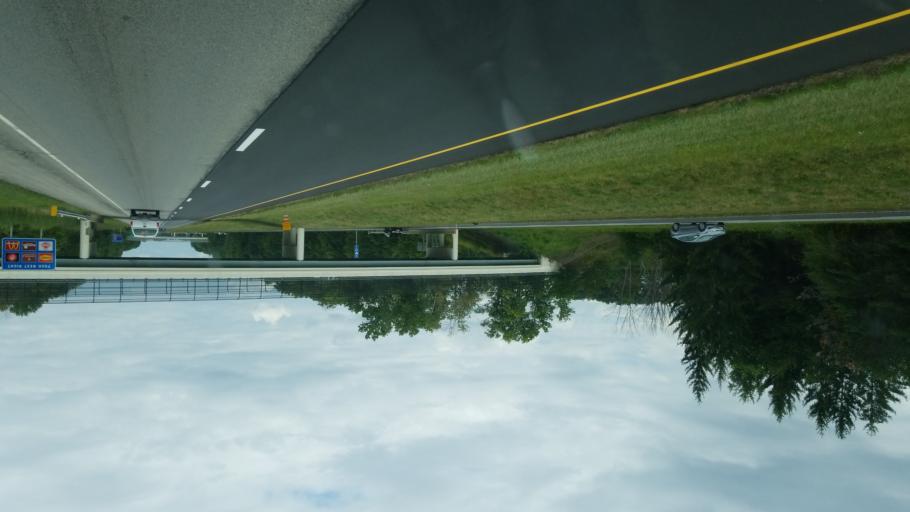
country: US
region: Ohio
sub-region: Mahoning County
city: Austintown
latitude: 41.0830
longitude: -80.7519
